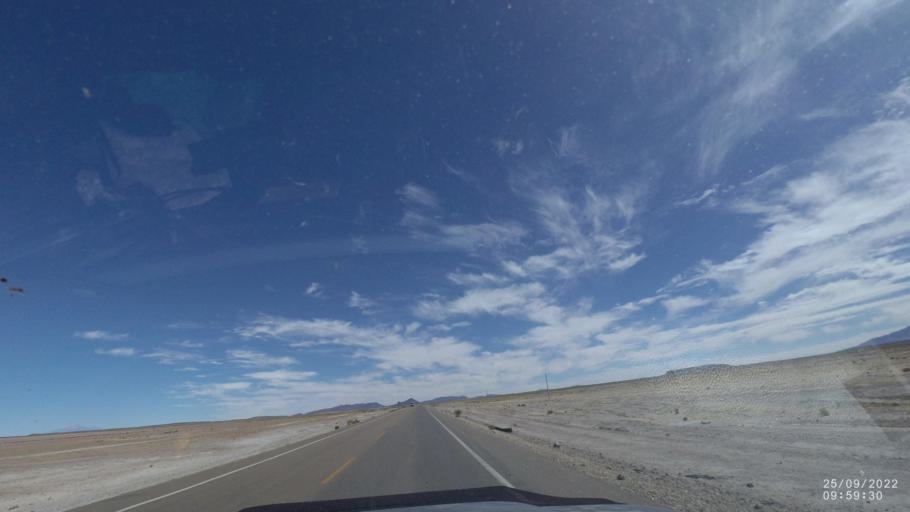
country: BO
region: Potosi
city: Colchani
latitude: -20.2910
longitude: -66.9382
